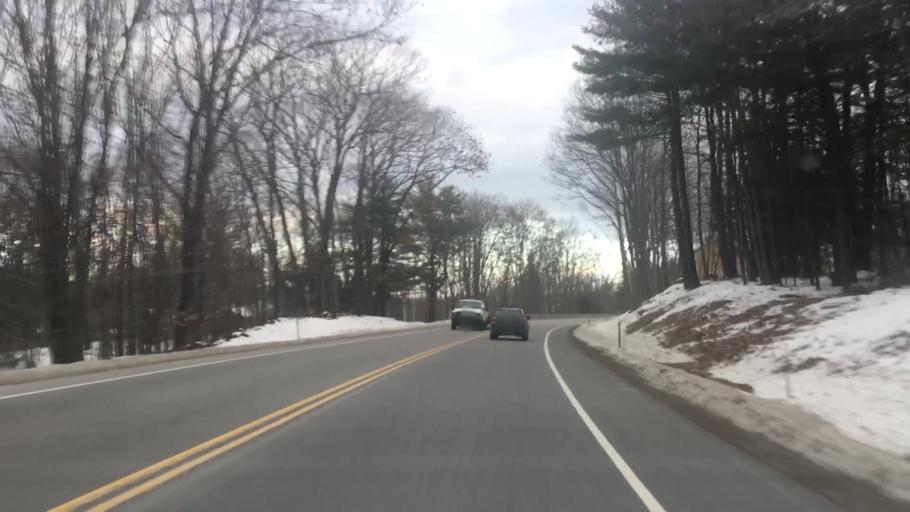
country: US
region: New Hampshire
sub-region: Hillsborough County
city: Antrim
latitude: 43.0799
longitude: -71.9787
